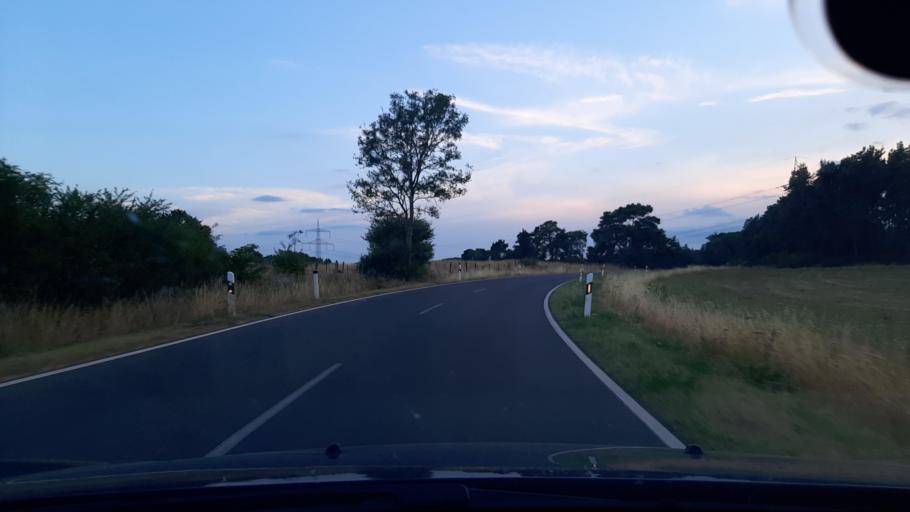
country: DE
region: North Rhine-Westphalia
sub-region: Regierungsbezirk Koln
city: Kall
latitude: 50.5515
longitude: 6.6057
